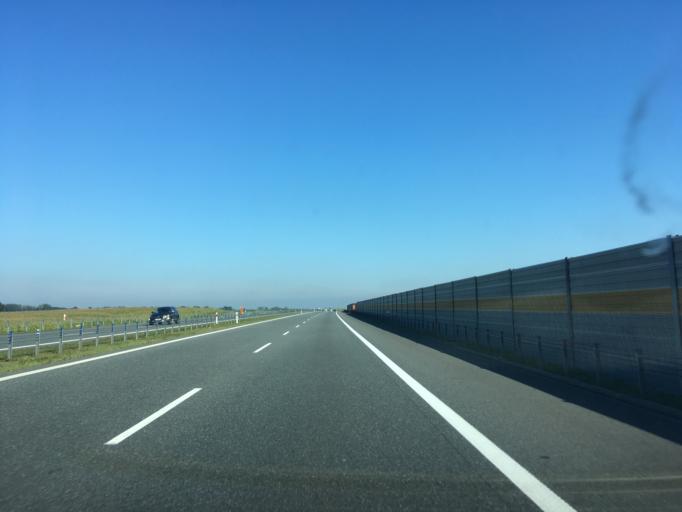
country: PL
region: Kujawsko-Pomorskie
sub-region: Powiat wabrzeski
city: Pluznica
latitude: 53.1898
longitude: 18.7380
